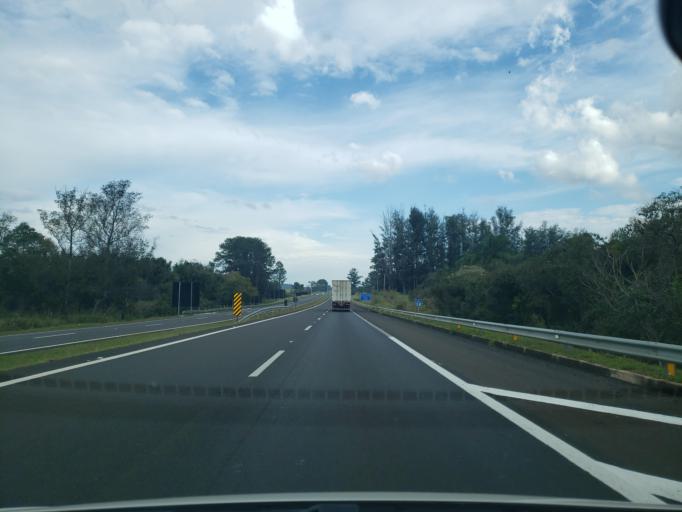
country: BR
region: Sao Paulo
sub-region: Itirapina
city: Itirapina
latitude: -22.2646
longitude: -47.9105
